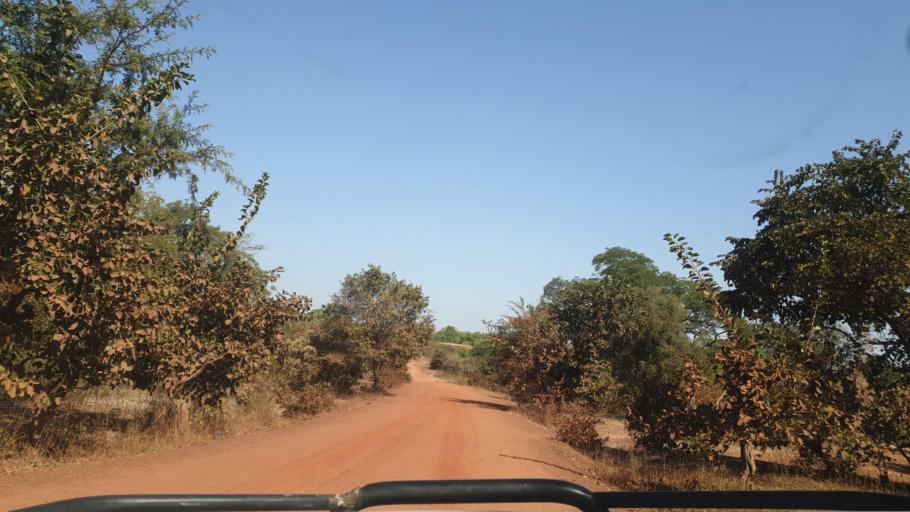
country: ML
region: Koulikoro
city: Dioila
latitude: 11.8929
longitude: -6.9805
